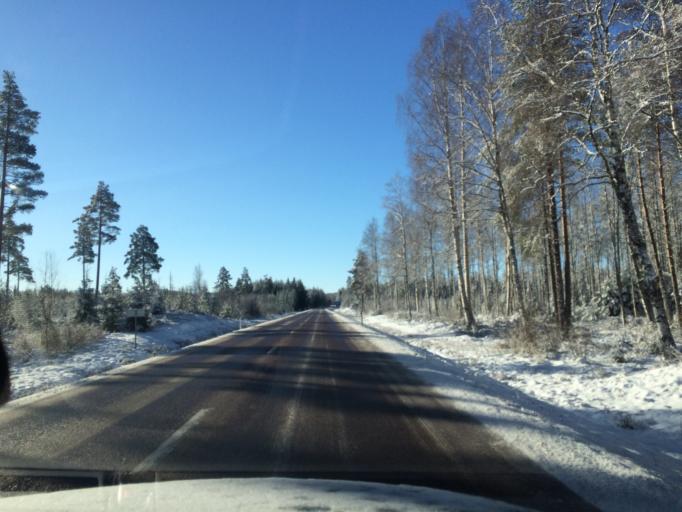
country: SE
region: Dalarna
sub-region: Mora Kommun
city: Mora
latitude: 60.9326
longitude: 14.4720
